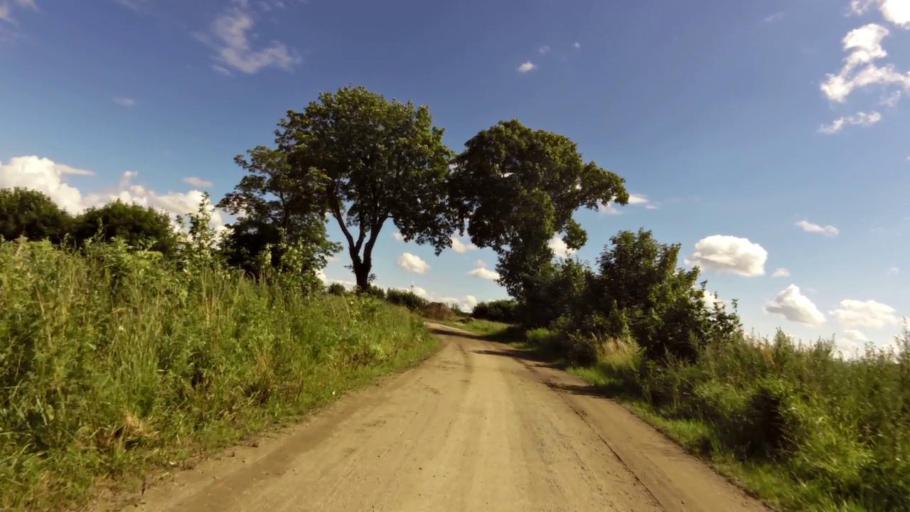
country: PL
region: Pomeranian Voivodeship
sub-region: Powiat slupski
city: Ustka
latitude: 54.5166
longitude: 16.7289
